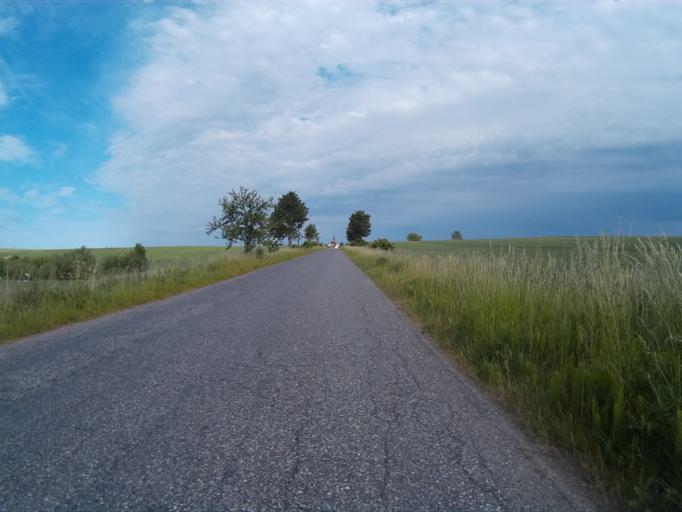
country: PL
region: Kujawsko-Pomorskie
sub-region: Powiat tucholski
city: Lubiewo
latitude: 53.4675
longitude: 18.0090
